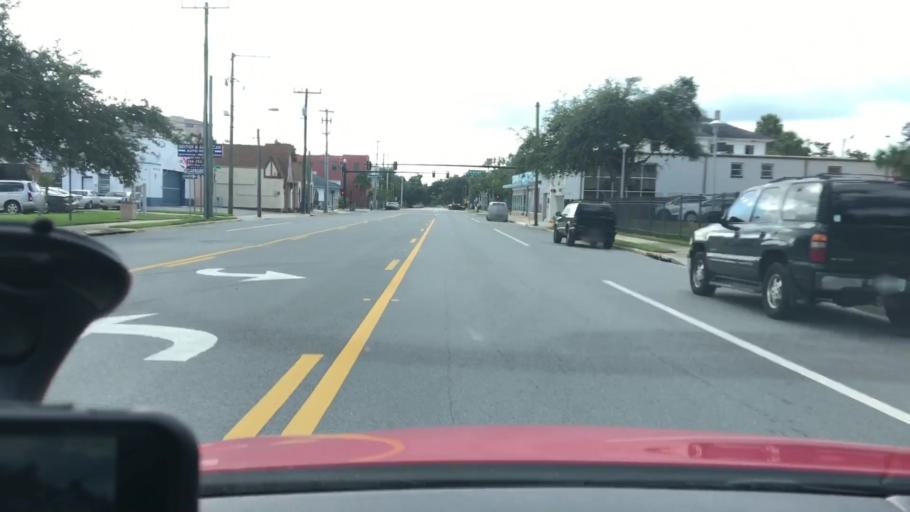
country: US
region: Florida
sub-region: Volusia County
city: Daytona Beach
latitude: 29.2087
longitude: -81.0199
